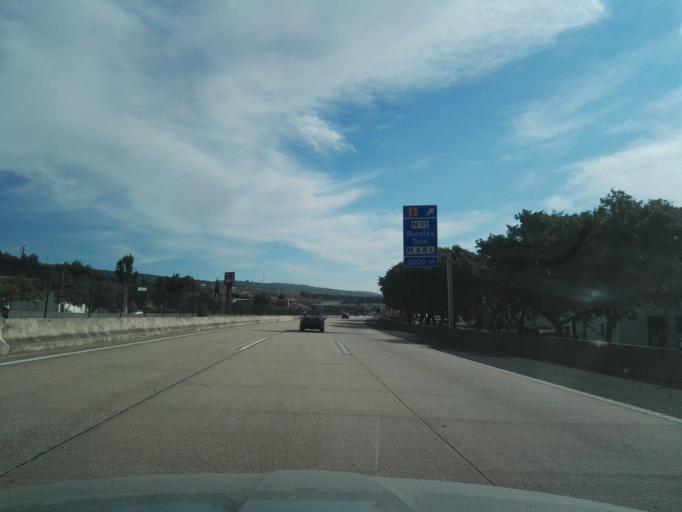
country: PT
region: Lisbon
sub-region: Loures
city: Santo Antao do Tojal
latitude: 38.8587
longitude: -9.1620
